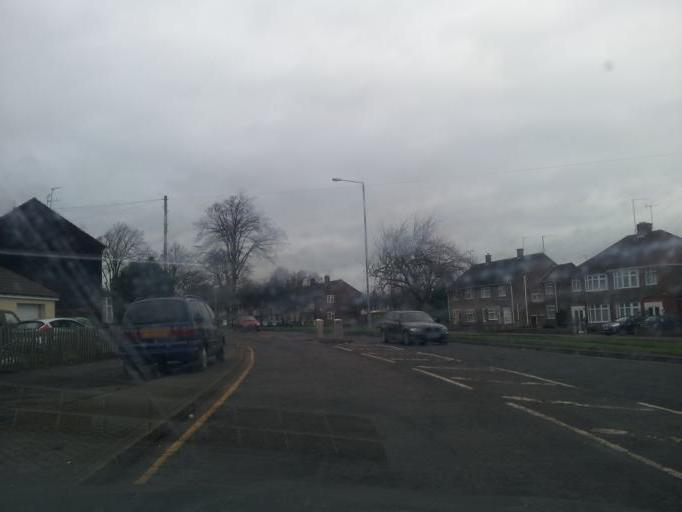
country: GB
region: England
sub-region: Northamptonshire
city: Kettering
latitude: 52.3994
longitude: -0.7117
